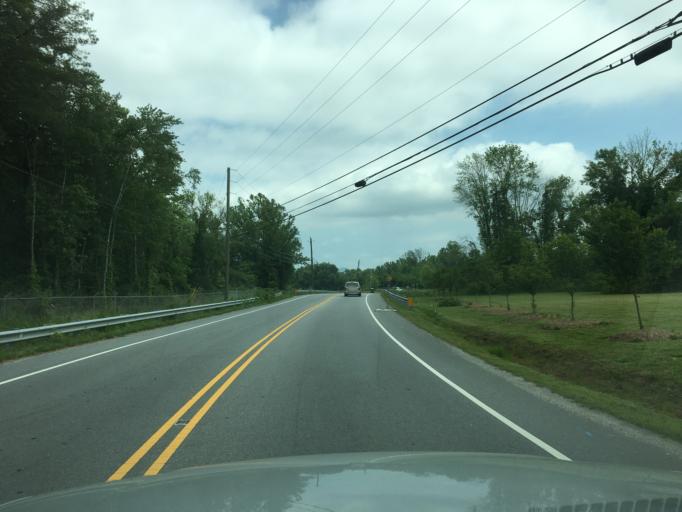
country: US
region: North Carolina
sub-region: Henderson County
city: Fletcher
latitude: 35.4187
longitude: -82.4998
